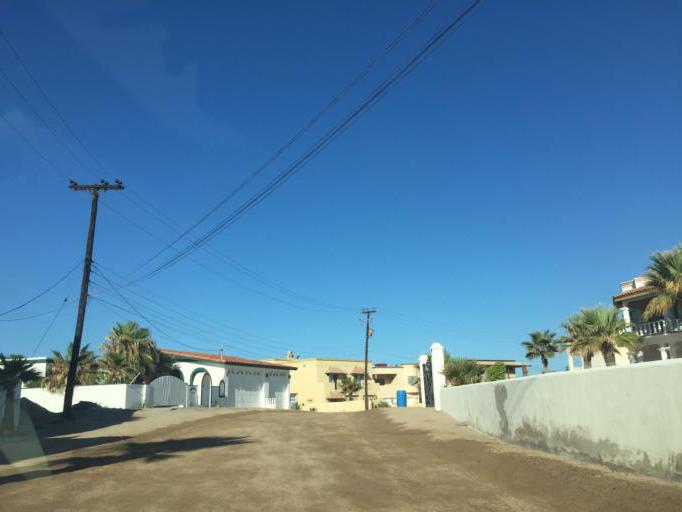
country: MX
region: Sonora
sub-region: Puerto Penasco
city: Puerto Penasco
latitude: 31.2898
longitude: -113.4904
